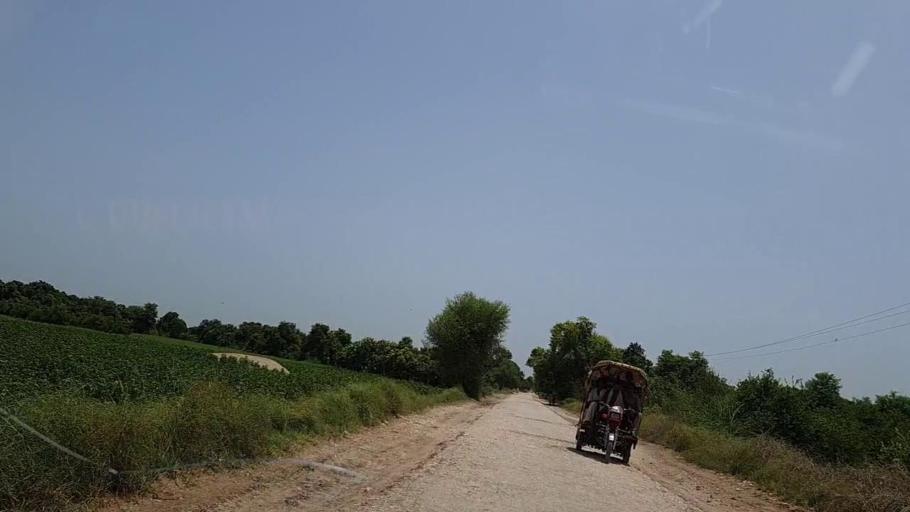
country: PK
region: Sindh
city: Tharu Shah
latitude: 26.9493
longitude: 68.0977
